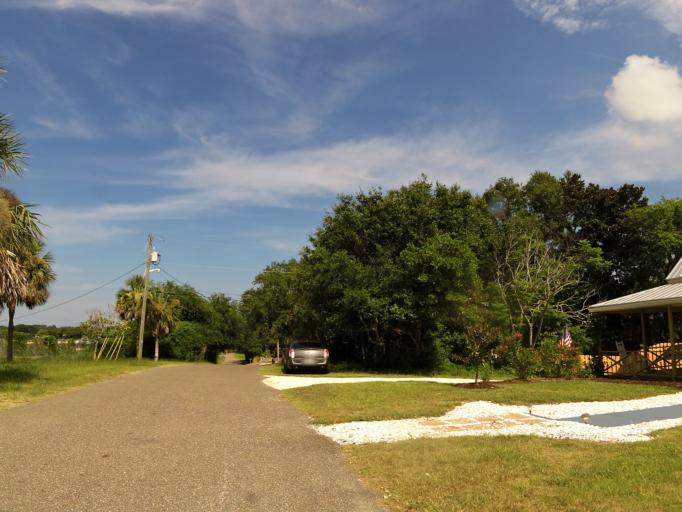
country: US
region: Florida
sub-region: Nassau County
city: Fernandina Beach
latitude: 30.6774
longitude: -81.4616
